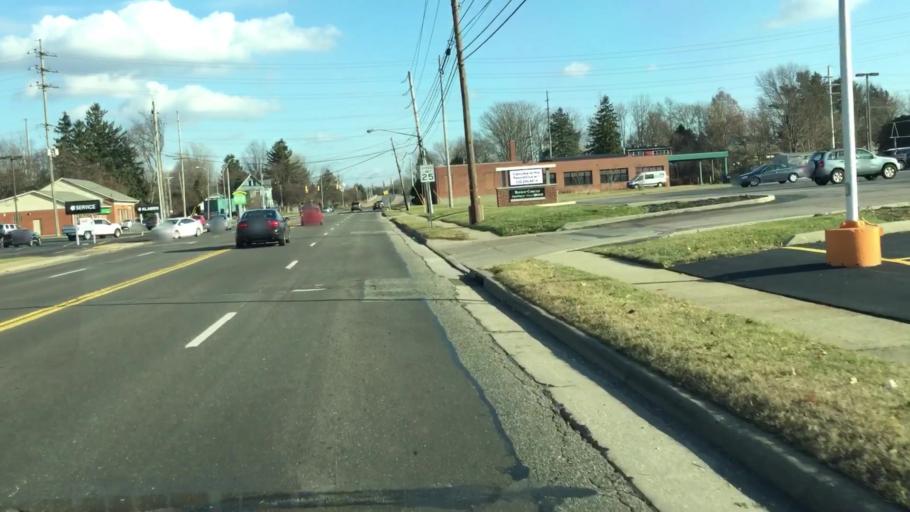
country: US
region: Ohio
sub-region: Portage County
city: Kent
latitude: 41.1514
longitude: -81.3798
